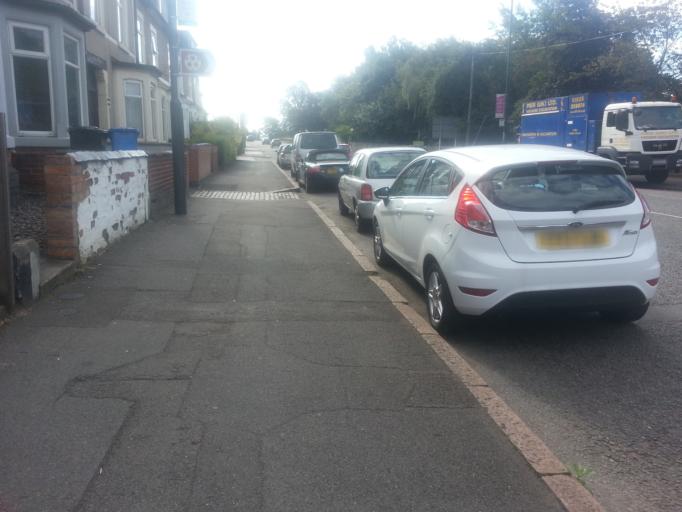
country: GB
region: England
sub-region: Derby
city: Derby
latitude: 52.9051
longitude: -1.4478
